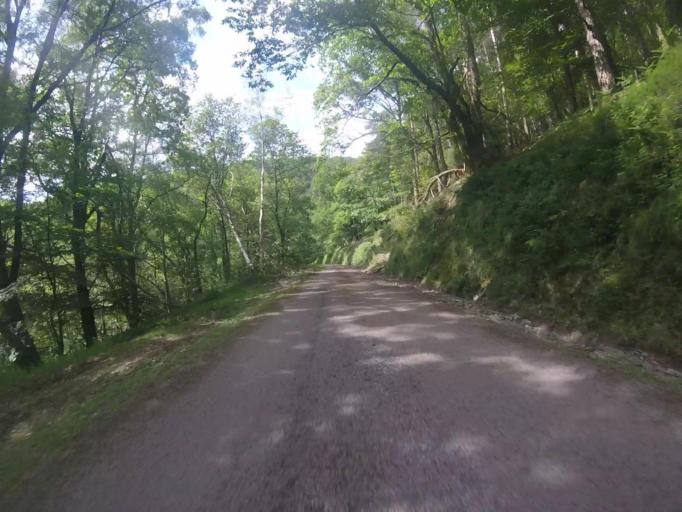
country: ES
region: Navarre
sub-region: Provincia de Navarra
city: Goizueta
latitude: 43.2207
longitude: -1.8033
